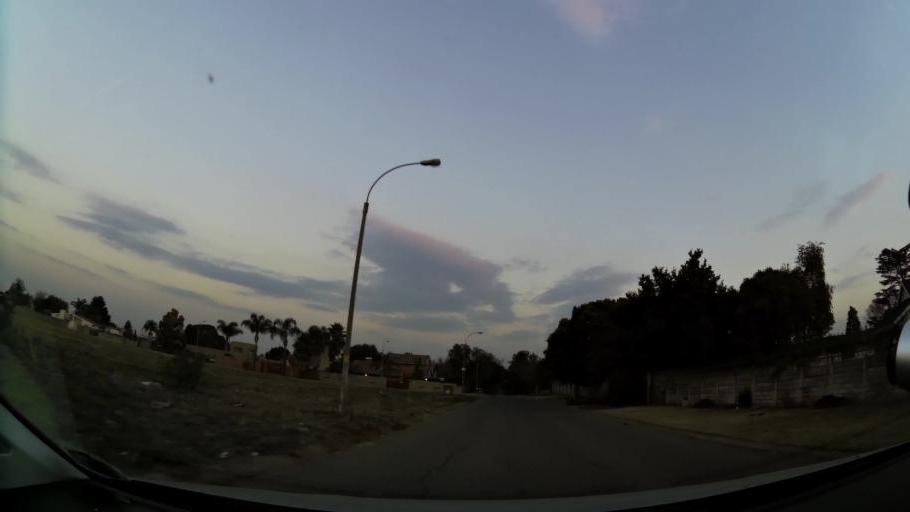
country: ZA
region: Gauteng
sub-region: Ekurhuleni Metropolitan Municipality
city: Tembisa
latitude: -26.0517
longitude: 28.2413
